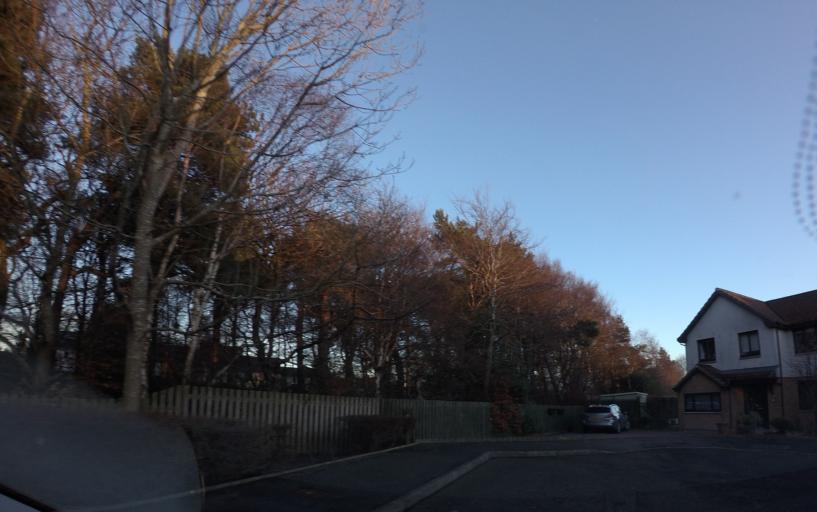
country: GB
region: Scotland
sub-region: West Lothian
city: Livingston
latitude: 55.9021
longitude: -3.5361
